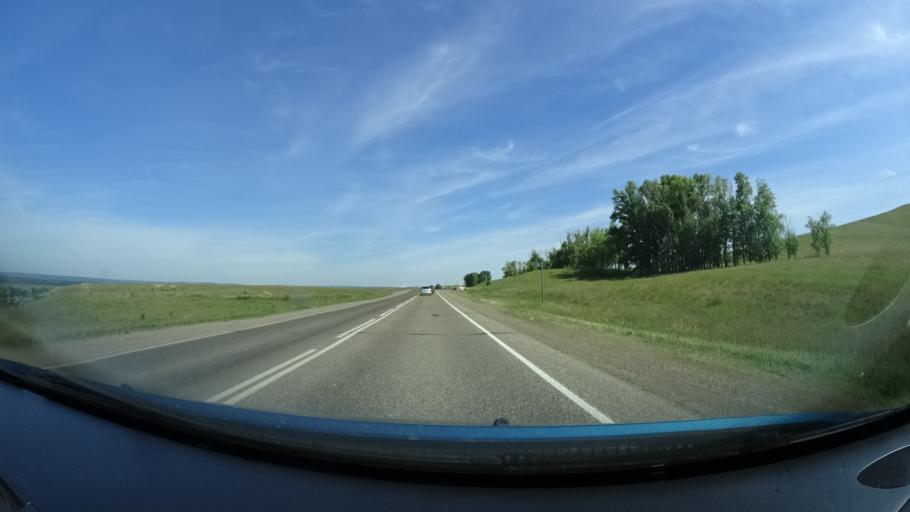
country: RU
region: Bashkortostan
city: Blagoveshchensk
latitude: 55.1684
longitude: 55.8534
